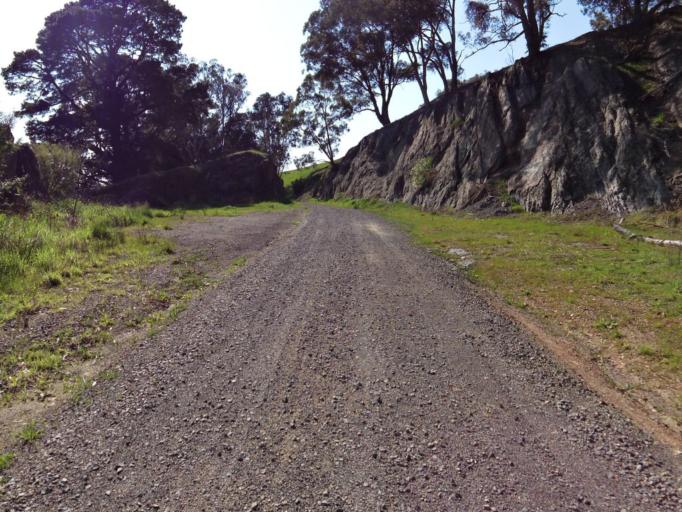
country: AU
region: Victoria
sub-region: Murrindindi
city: Alexandra
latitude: -37.1689
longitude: 145.5401
